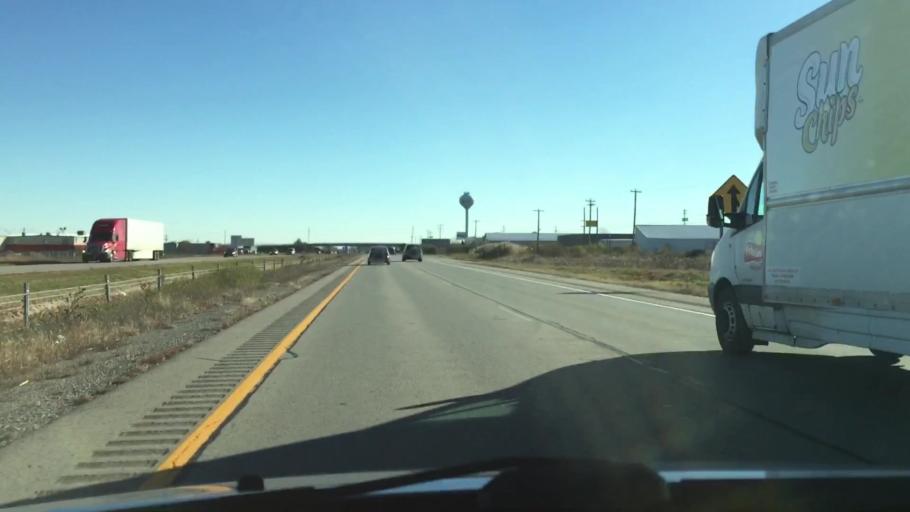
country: US
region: Wisconsin
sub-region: Outagamie County
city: Little Chute
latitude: 44.2977
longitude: -88.3107
